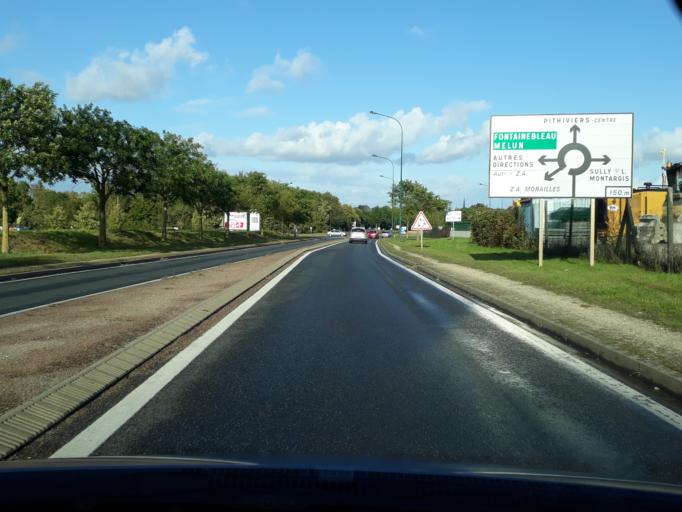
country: FR
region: Centre
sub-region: Departement du Loiret
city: Pithiviers
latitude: 48.1589
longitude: 2.2330
